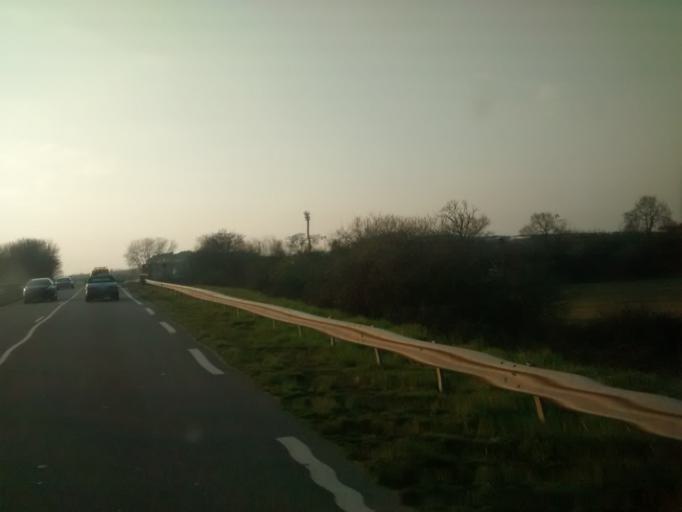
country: FR
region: Brittany
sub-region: Departement d'Ille-et-Vilaine
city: Saint-Jacques-de-la-Lande
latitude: 48.0537
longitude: -1.7274
